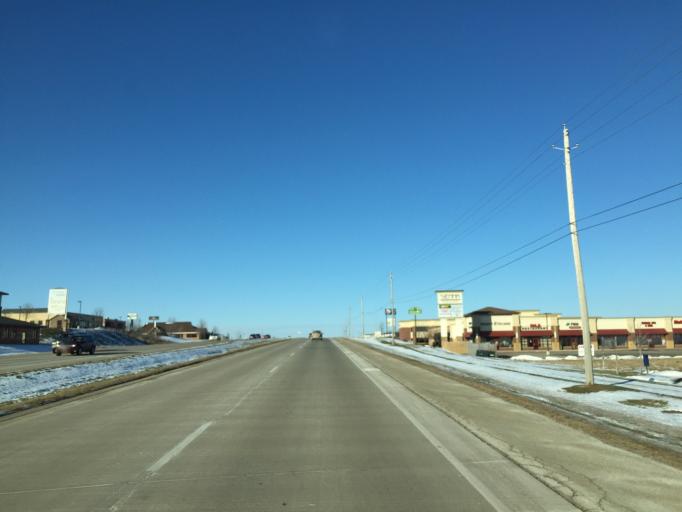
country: US
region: Minnesota
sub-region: Olmsted County
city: Rochester
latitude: 44.0511
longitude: -92.5221
